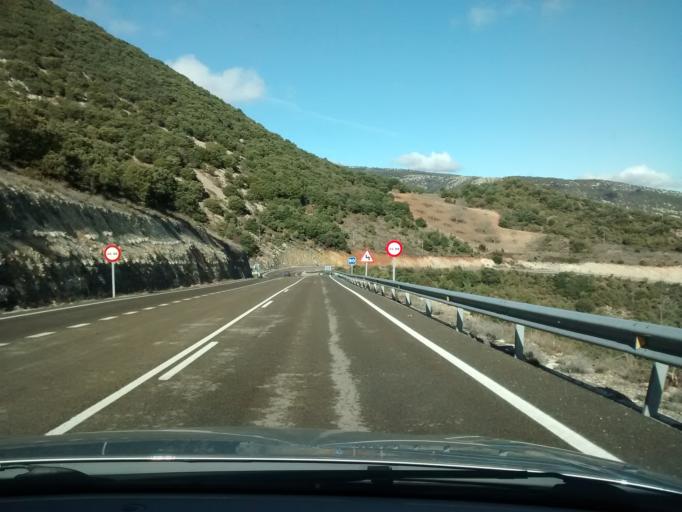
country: ES
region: Castille and Leon
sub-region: Provincia de Burgos
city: Rucandio
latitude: 42.8335
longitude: -3.6140
